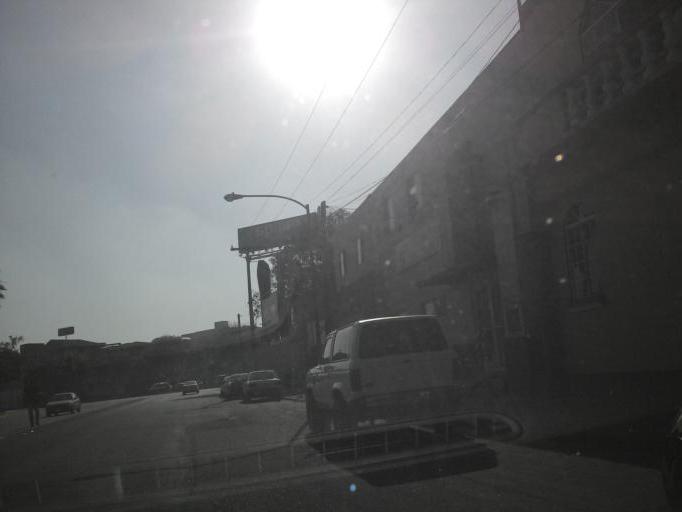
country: MX
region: Baja California
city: Tijuana
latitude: 32.5251
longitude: -117.0245
